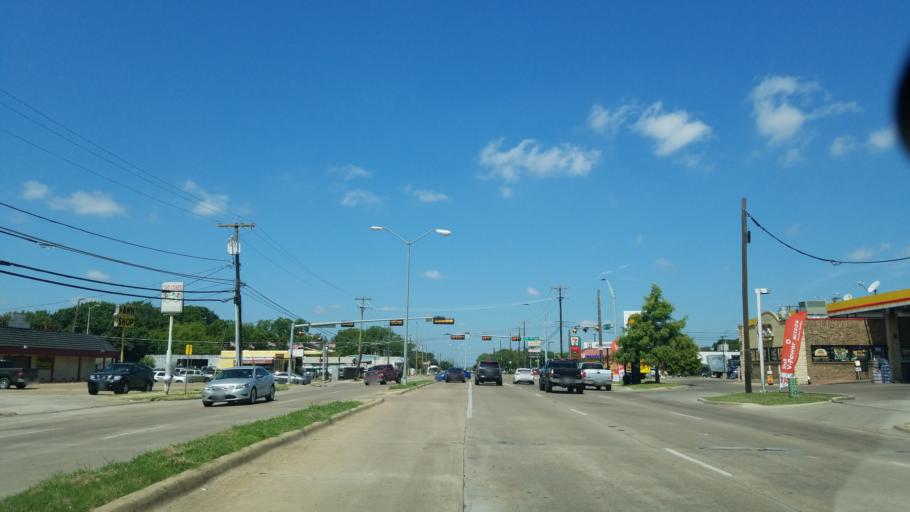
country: US
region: Texas
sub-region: Dallas County
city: Balch Springs
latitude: 32.7343
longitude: -96.6992
